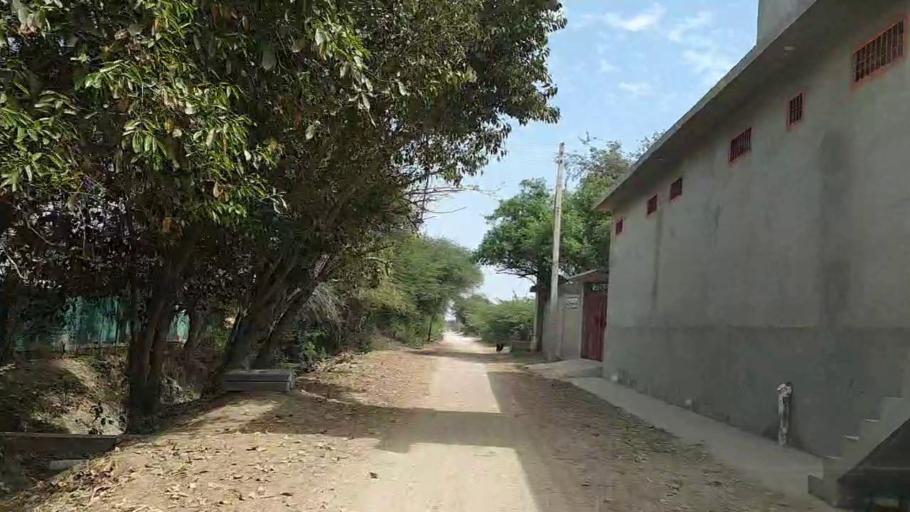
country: PK
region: Sindh
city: Daro Mehar
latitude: 24.7753
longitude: 68.2090
